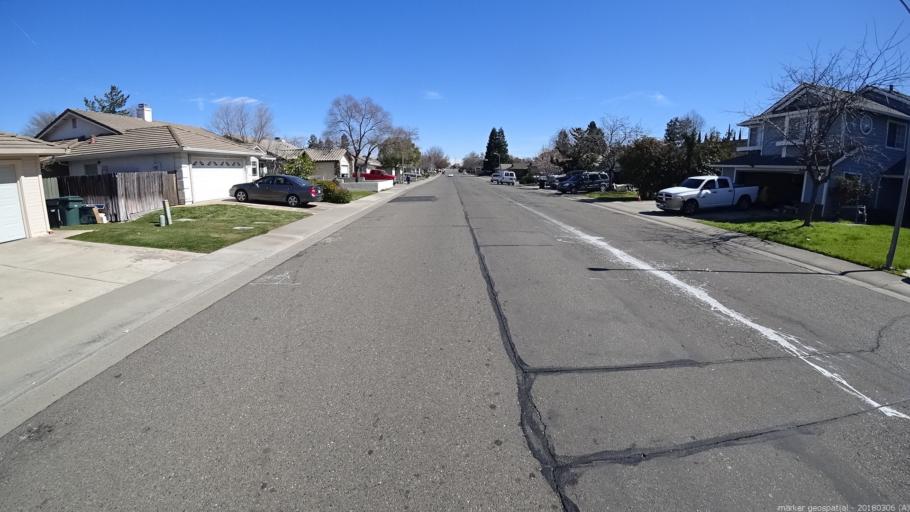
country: US
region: California
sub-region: Sacramento County
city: Vineyard
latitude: 38.4671
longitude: -121.3642
